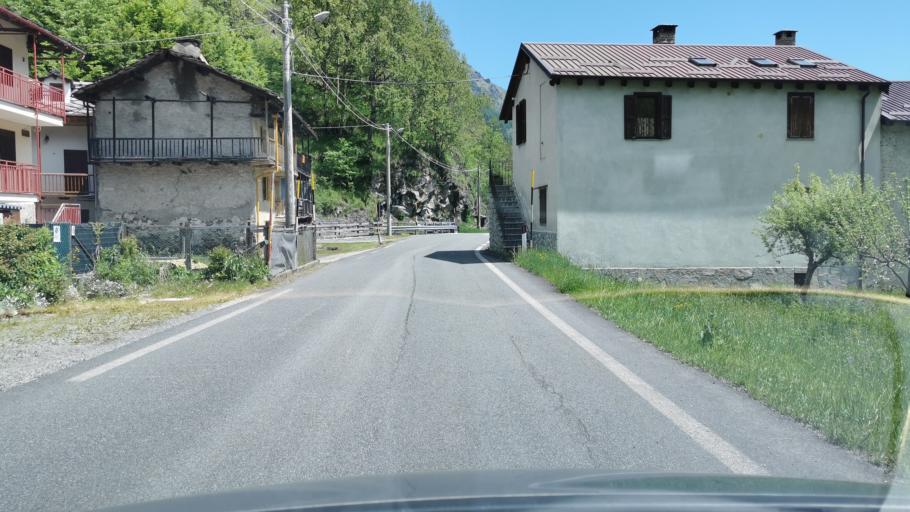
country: IT
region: Piedmont
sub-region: Provincia di Torino
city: Usseglio
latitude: 45.2313
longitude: 7.2044
